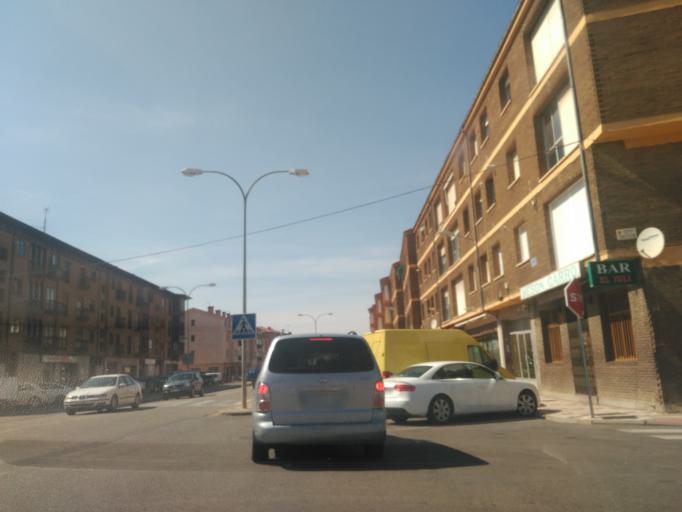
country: ES
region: Castille and Leon
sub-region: Provincia de Soria
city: El Burgo de Osma
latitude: 41.5878
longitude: -3.0684
